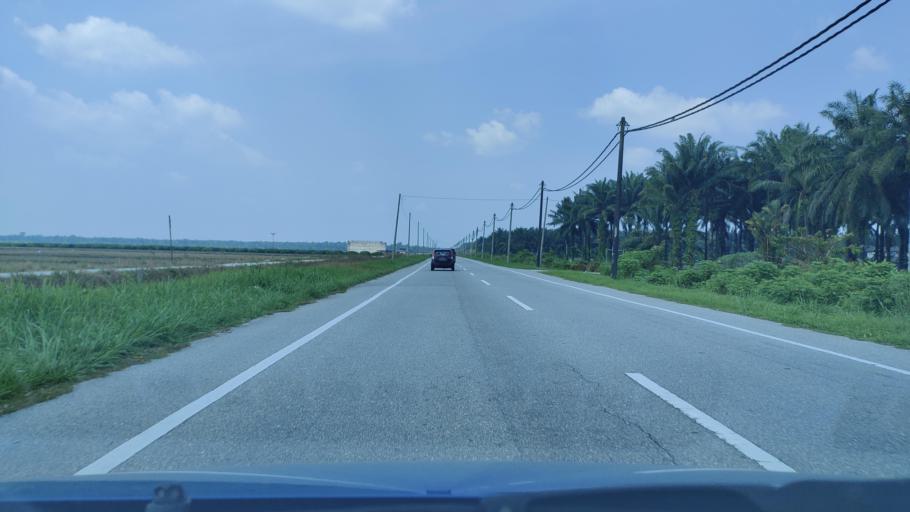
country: MY
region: Perak
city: Tapah Road
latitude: 4.0481
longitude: 101.1660
